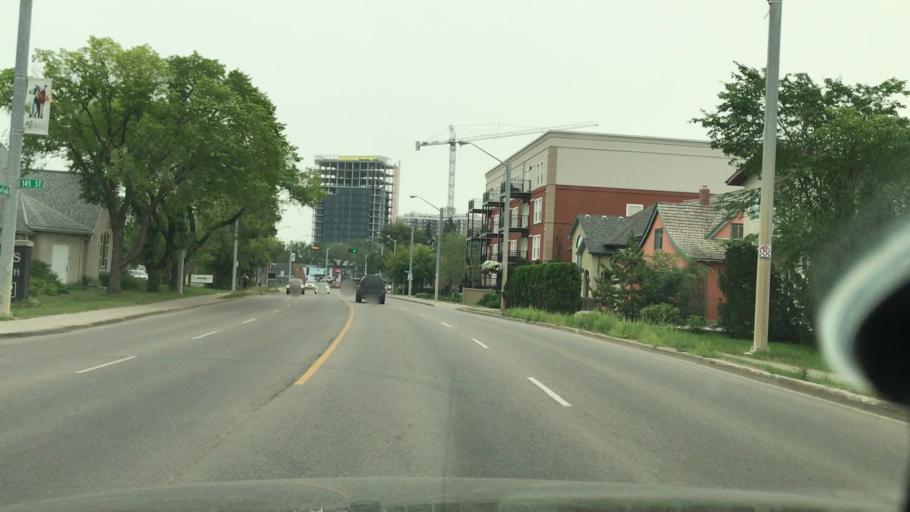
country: CA
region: Alberta
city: Edmonton
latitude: 53.5420
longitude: -113.5709
